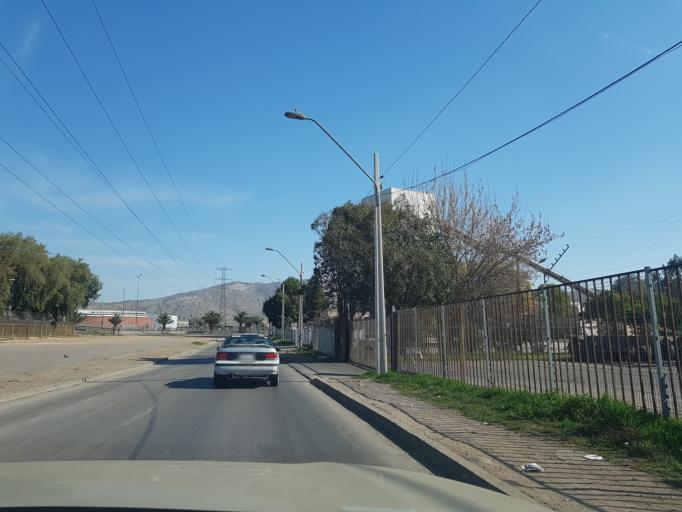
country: CL
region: Santiago Metropolitan
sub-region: Provincia de Santiago
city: Lo Prado
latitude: -33.3720
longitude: -70.7224
